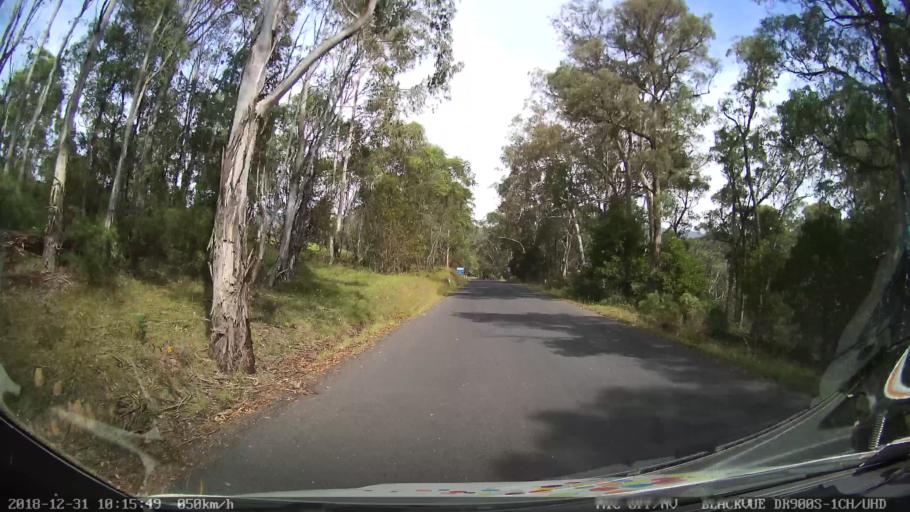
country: AU
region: New South Wales
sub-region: Snowy River
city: Jindabyne
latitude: -36.5415
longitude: 148.1408
